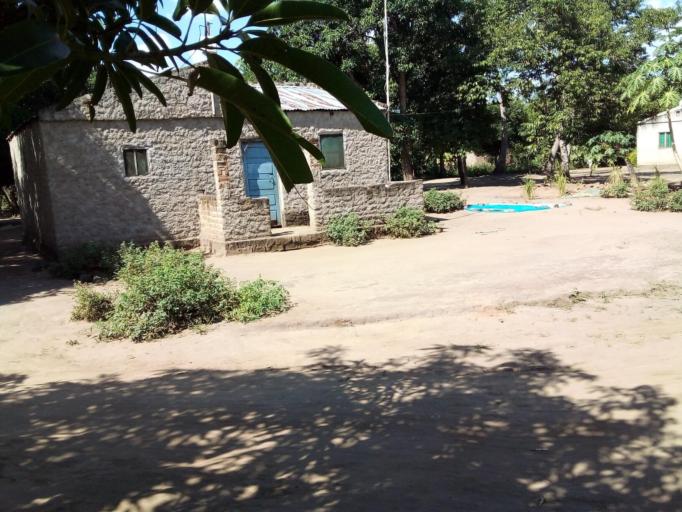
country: MZ
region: Zambezia
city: Quelimane
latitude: -17.5815
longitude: 36.6956
